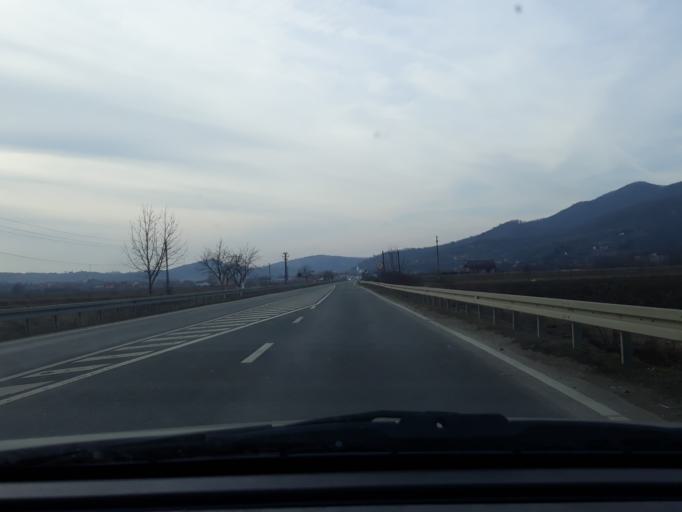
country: RO
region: Salaj
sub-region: Oras Simleu Silvaniei
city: Simleu Silvaniei
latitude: 47.2294
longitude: 22.8328
